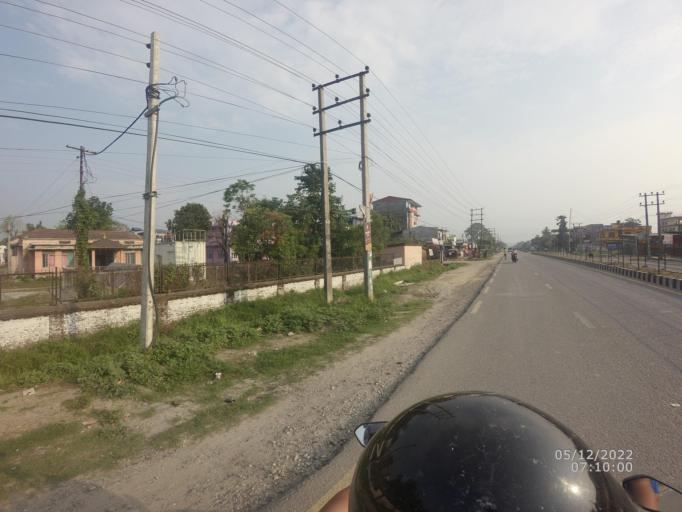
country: NP
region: Central Region
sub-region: Narayani Zone
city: Bharatpur
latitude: 27.6725
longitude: 84.4386
